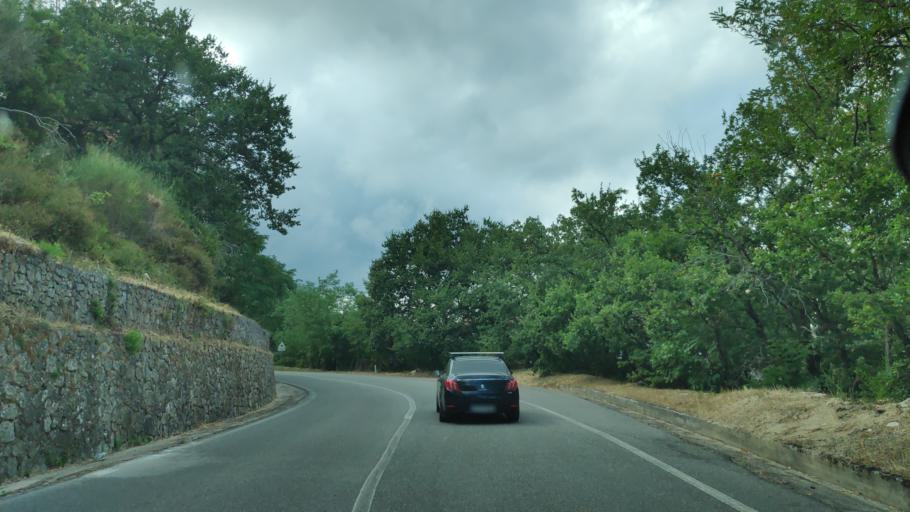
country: IT
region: Calabria
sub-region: Provincia di Catanzaro
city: Santa Caterina dello Ionio
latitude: 38.5307
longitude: 16.5232
